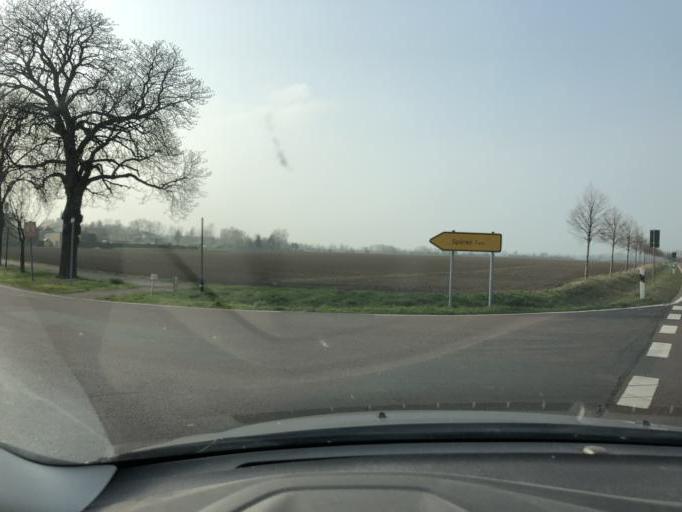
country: DE
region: Saxony-Anhalt
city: Zorbig
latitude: 51.6013
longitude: 12.1310
